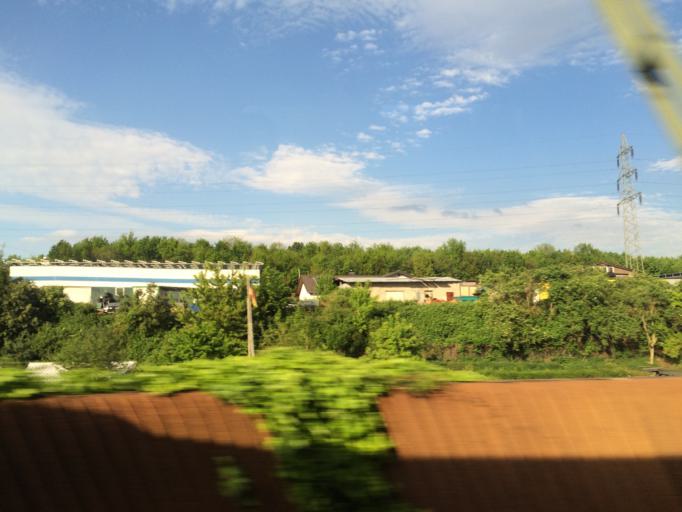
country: DE
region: North Rhine-Westphalia
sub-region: Regierungsbezirk Koln
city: Leverkusen
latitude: 51.0517
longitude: 6.9855
